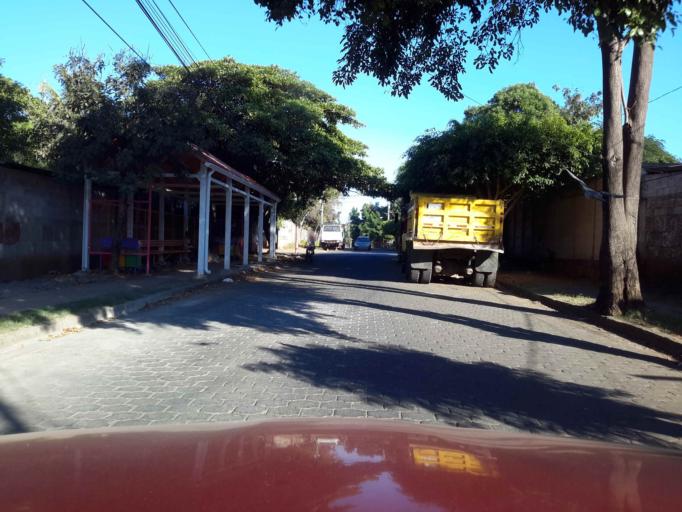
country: NI
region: Managua
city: Managua
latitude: 12.1239
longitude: -86.2941
